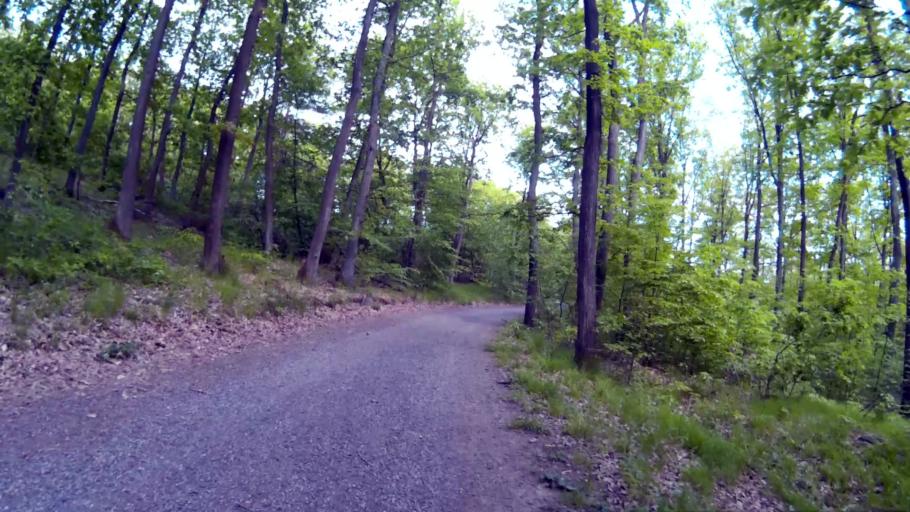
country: CZ
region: South Moravian
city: Troubsko
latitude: 49.1910
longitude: 16.5243
